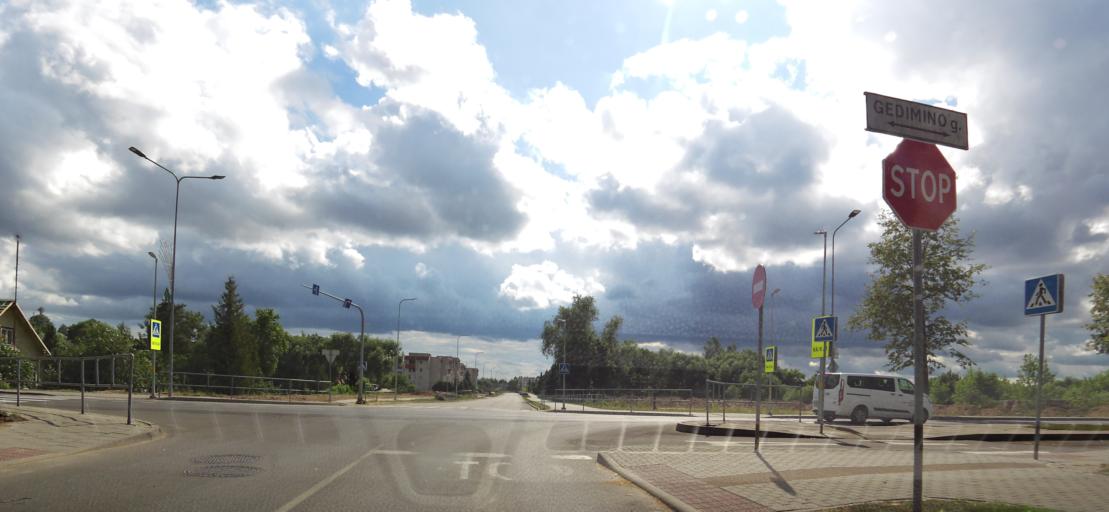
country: LT
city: Kupiskis
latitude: 55.8347
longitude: 24.9796
